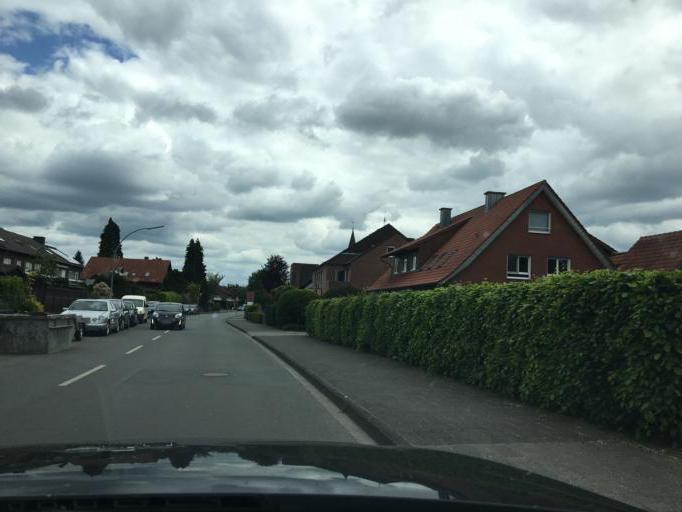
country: DE
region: North Rhine-Westphalia
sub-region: Regierungsbezirk Munster
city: Muenster
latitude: 52.0313
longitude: 7.6752
